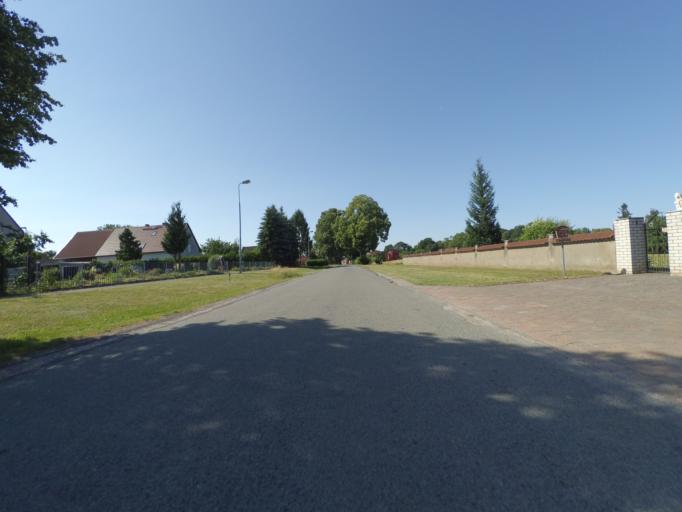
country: DE
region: Brandenburg
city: Triglitz
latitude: 53.2377
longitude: 12.1212
